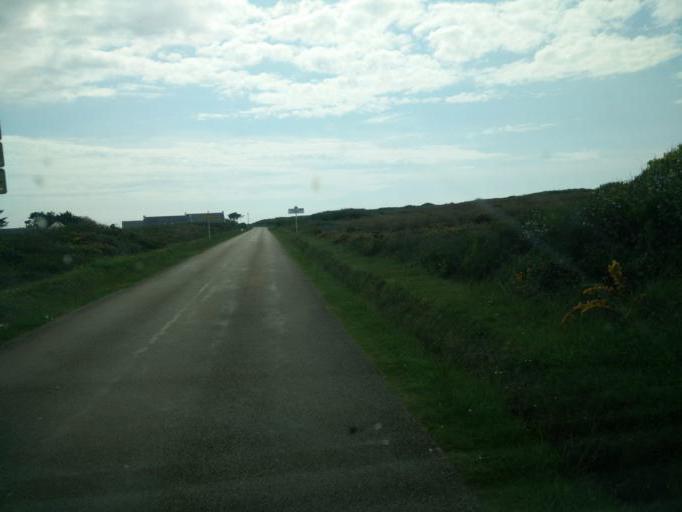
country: FR
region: Brittany
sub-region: Departement du Finistere
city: Camaret-sur-Mer
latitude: 48.2713
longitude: -4.6114
